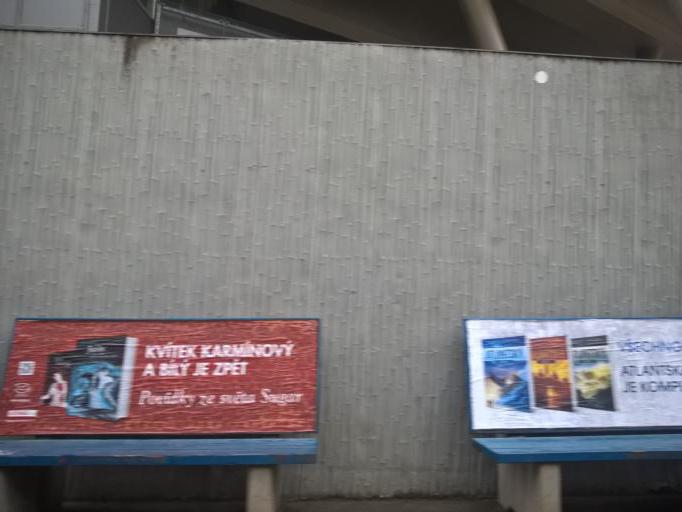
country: CZ
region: Praha
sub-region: Praha 1
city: Mala Strana
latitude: 50.0743
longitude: 14.3953
